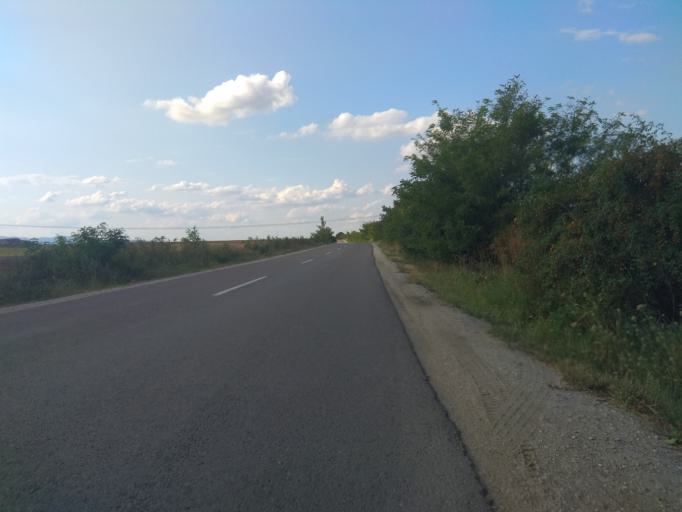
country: HU
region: Borsod-Abauj-Zemplen
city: Hejobaba
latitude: 47.9061
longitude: 20.8874
